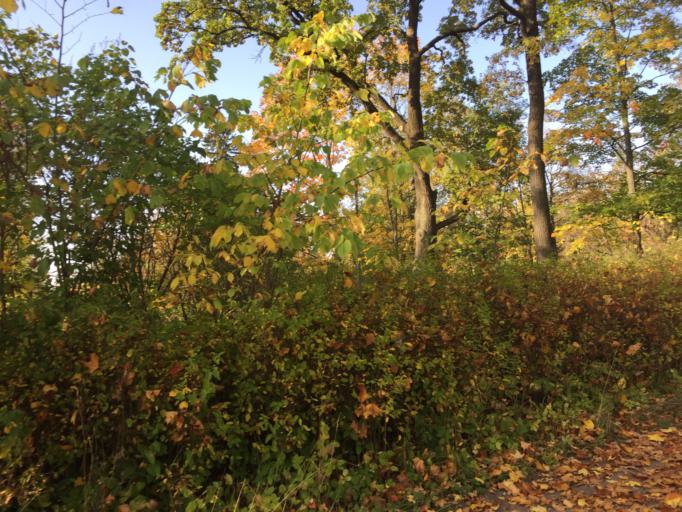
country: RU
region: St.-Petersburg
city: Pushkin
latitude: 59.7150
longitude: 30.3781
